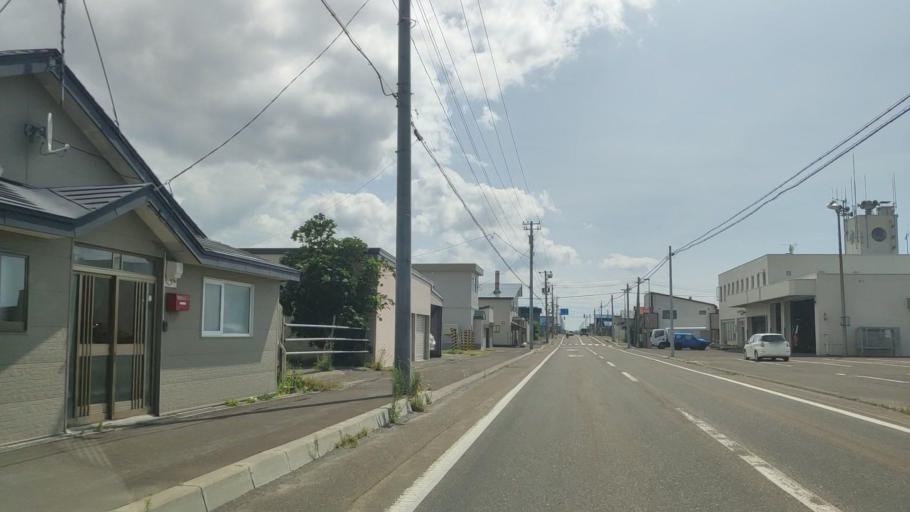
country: JP
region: Hokkaido
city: Makubetsu
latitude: 44.8846
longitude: 141.7426
